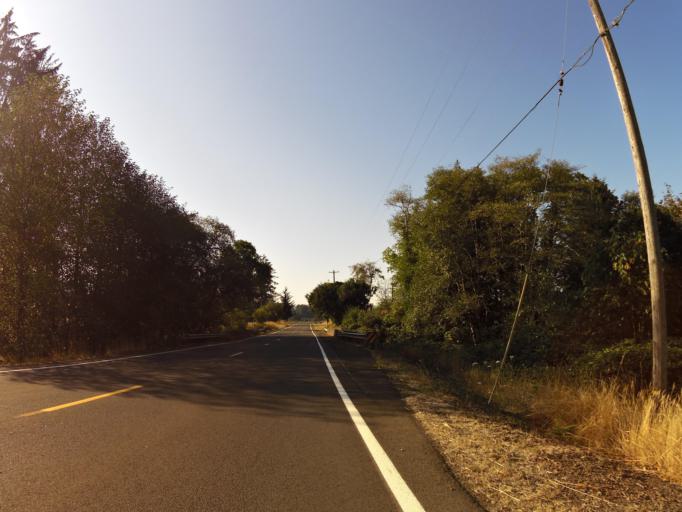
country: US
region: Oregon
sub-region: Tillamook County
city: Tillamook
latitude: 45.3964
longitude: -123.7931
